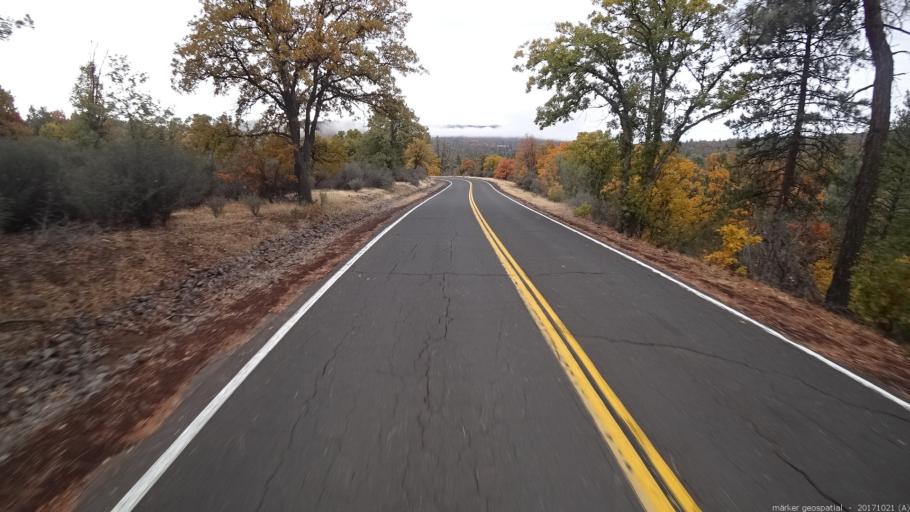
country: US
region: California
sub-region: Shasta County
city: Burney
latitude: 40.9964
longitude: -121.5042
